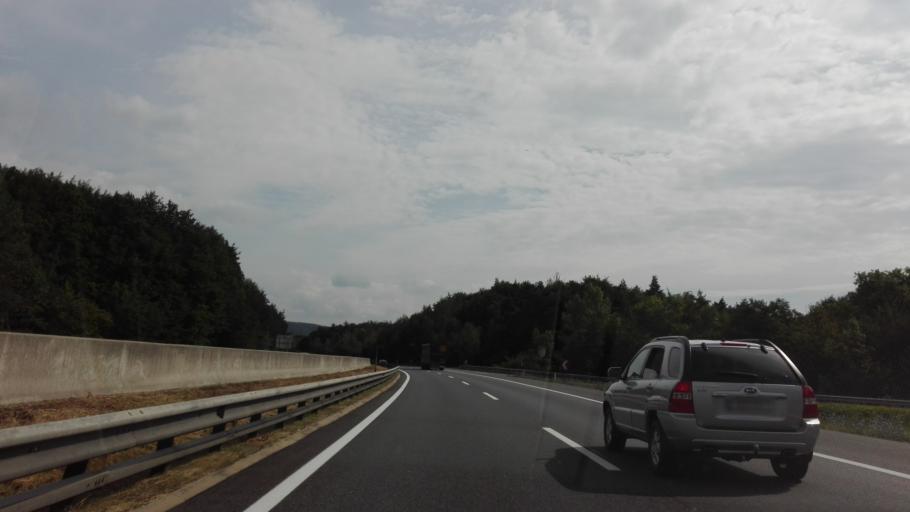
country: AT
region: Lower Austria
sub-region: Politischer Bezirk Baden
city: Heiligenkreuz
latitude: 48.0582
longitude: 16.1585
